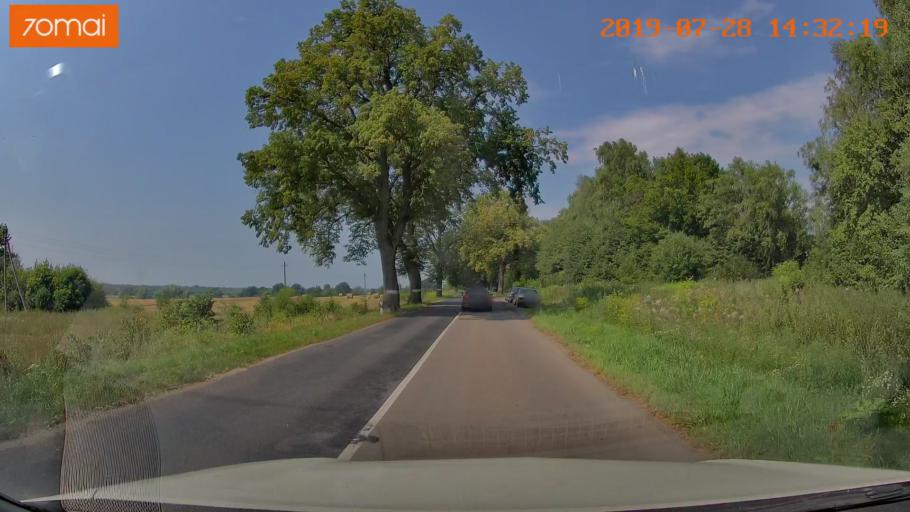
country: RU
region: Kaliningrad
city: Primorsk
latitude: 54.8119
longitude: 20.0428
